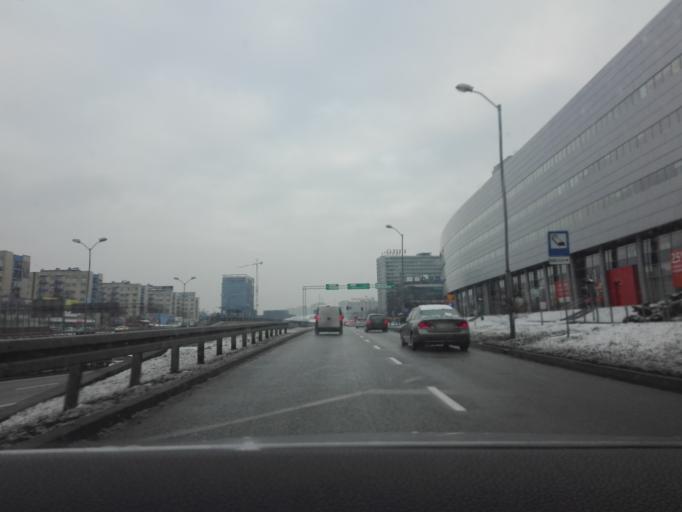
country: PL
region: Silesian Voivodeship
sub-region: Katowice
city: Katowice
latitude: 50.2658
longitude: 19.0162
